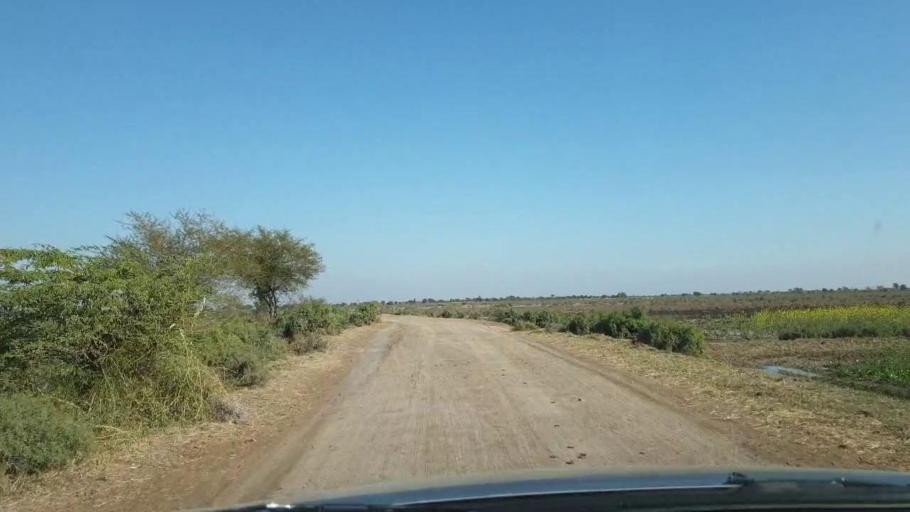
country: PK
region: Sindh
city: Jhol
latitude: 25.9167
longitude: 68.9820
